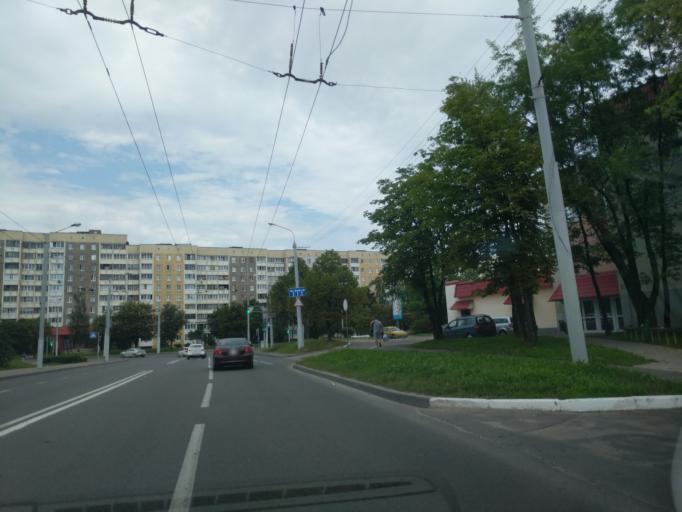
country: BY
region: Minsk
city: Novoye Medvezhino
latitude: 53.8928
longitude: 27.4844
